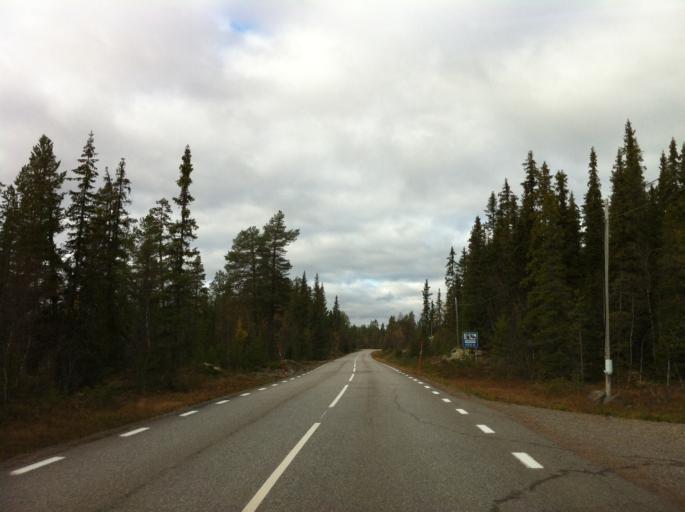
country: NO
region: Hedmark
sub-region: Engerdal
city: Engerdal
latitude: 61.9995
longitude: 12.4548
